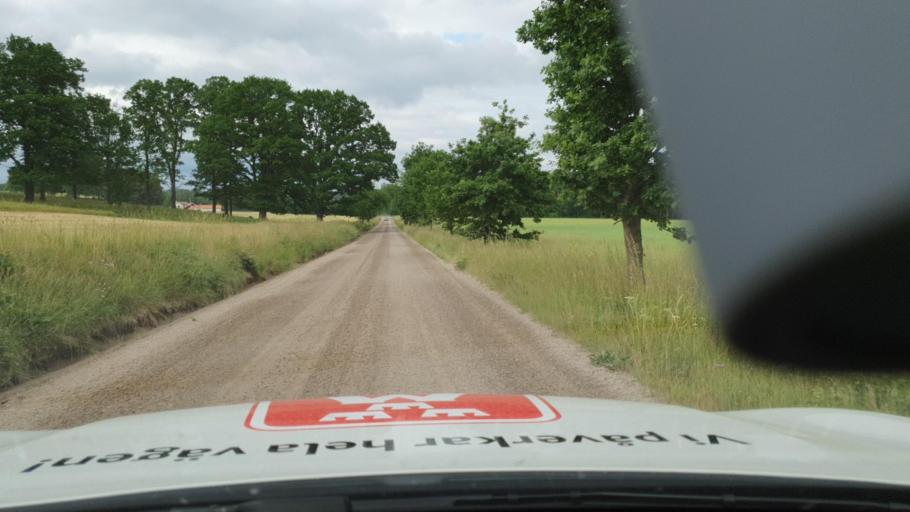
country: SE
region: Vaestra Goetaland
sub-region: Hjo Kommun
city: Hjo
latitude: 58.2191
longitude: 14.1999
